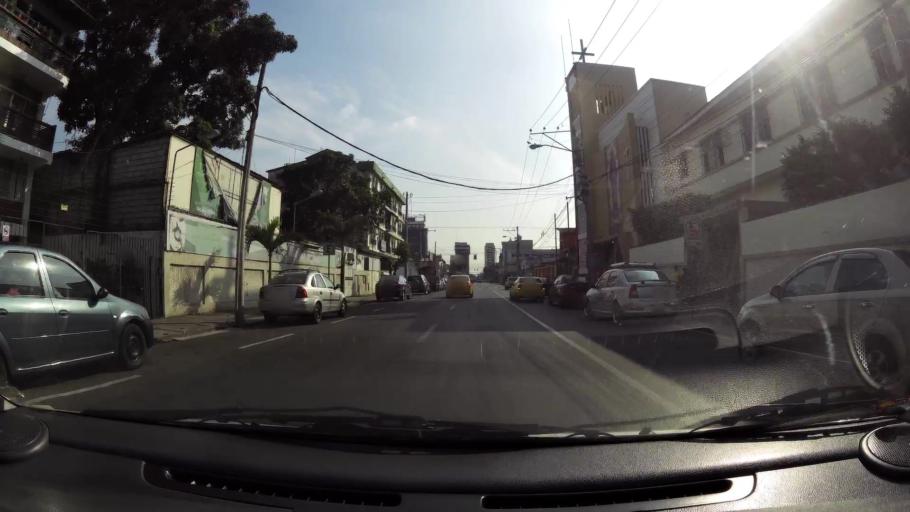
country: EC
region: Guayas
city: Guayaquil
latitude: -2.1912
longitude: -79.8967
